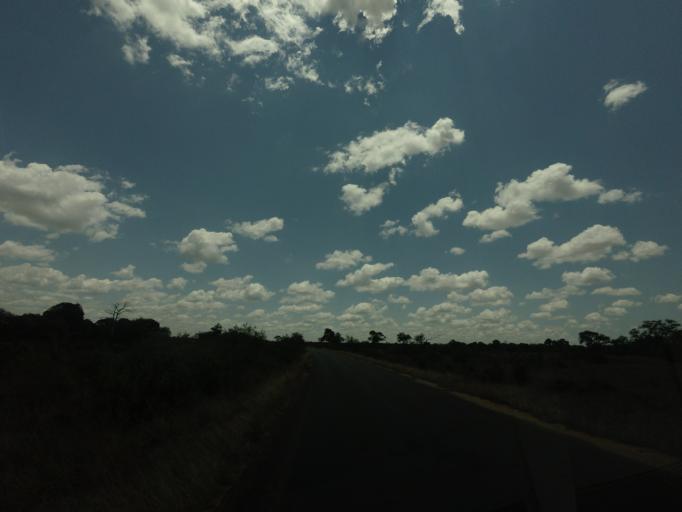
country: ZA
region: Limpopo
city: Thulamahashi
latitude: -24.6798
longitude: 31.8090
